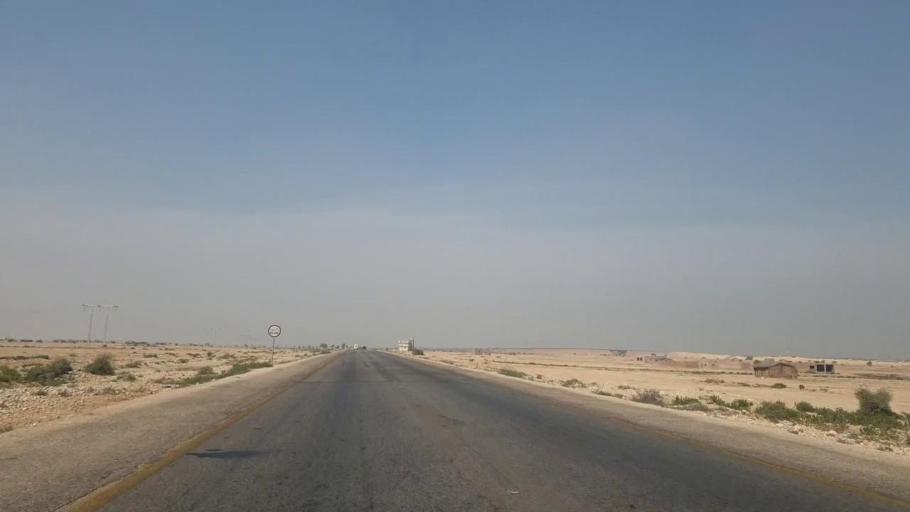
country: PK
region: Sindh
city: Hala
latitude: 25.8492
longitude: 68.2603
